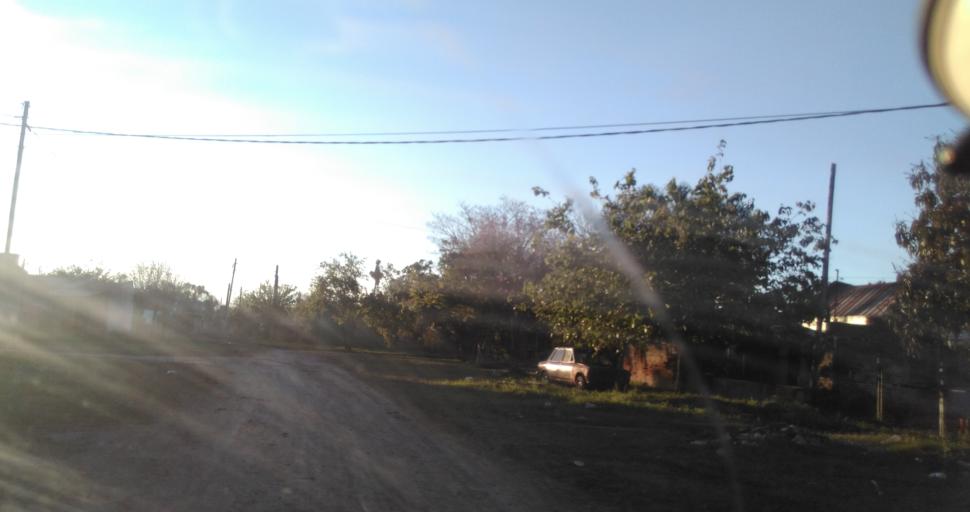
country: AR
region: Chaco
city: Fontana
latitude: -27.4242
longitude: -59.0253
